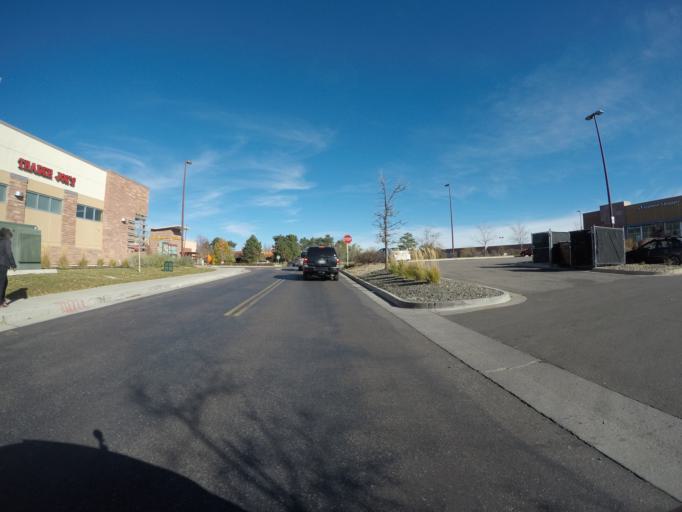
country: US
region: Colorado
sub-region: Boulder County
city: Boulder
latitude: 40.0201
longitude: -105.2573
